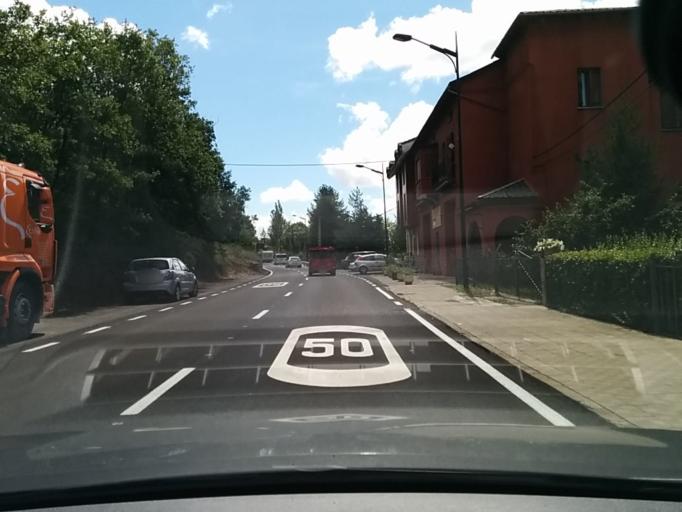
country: ES
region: Aragon
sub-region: Provincia de Huesca
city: Fiscal
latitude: 42.4985
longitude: -0.1153
